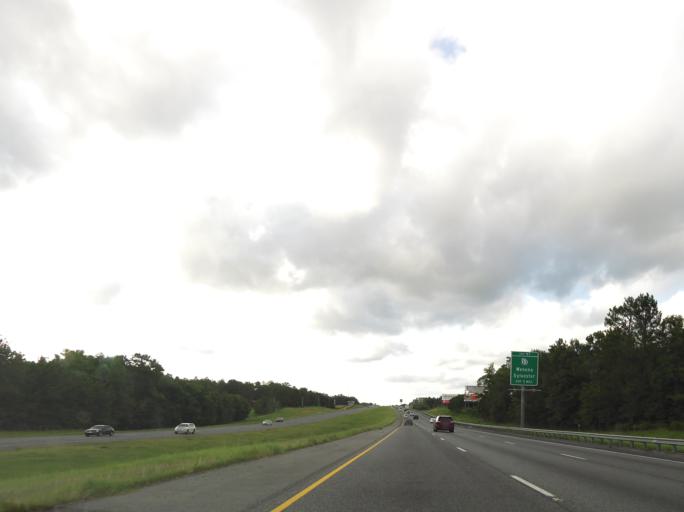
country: US
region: Georgia
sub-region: Crisp County
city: Cordele
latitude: 31.8909
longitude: -83.7312
